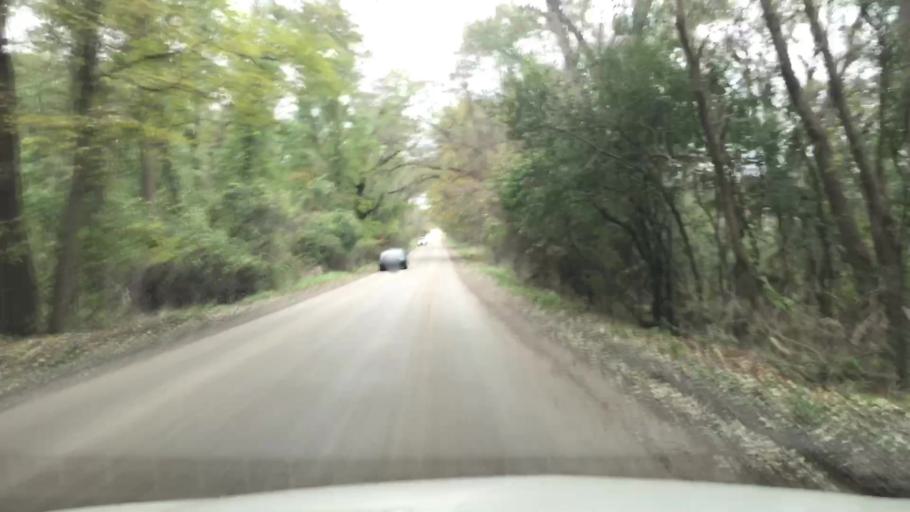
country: US
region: Michigan
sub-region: Oakland County
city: Rochester
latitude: 42.7339
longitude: -83.1042
